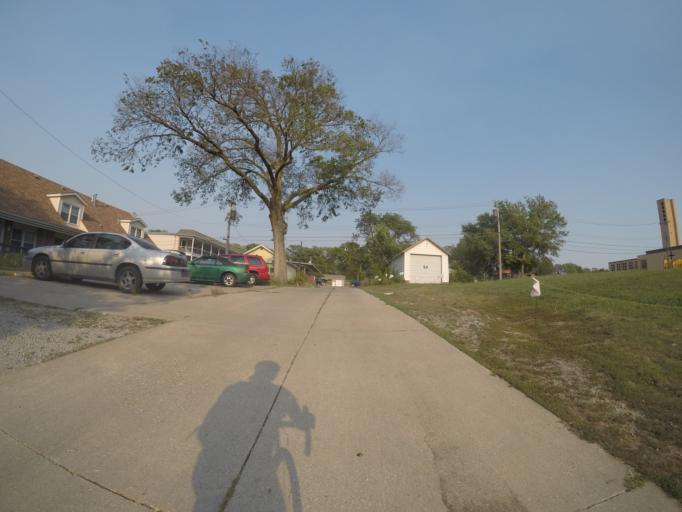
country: US
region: Nebraska
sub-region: Gage County
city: Beatrice
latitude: 40.2741
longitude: -96.7478
